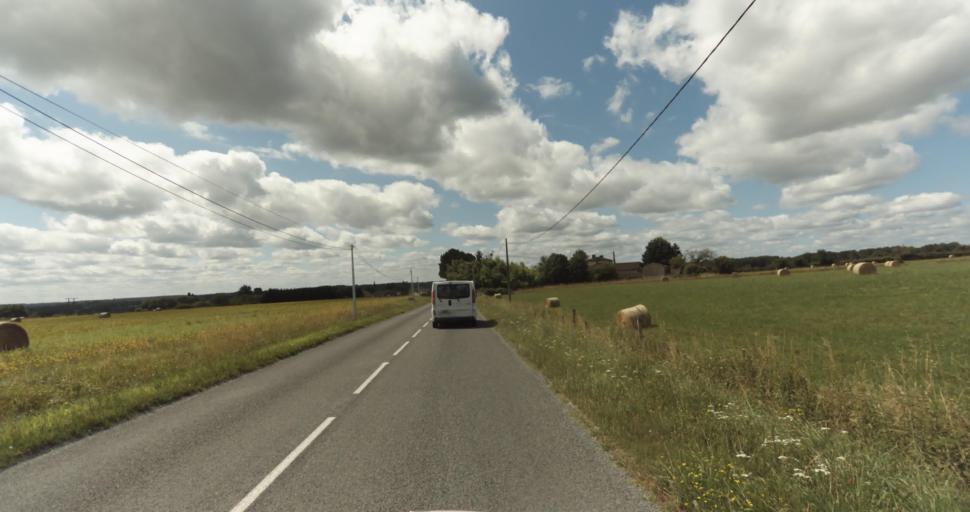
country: FR
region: Aquitaine
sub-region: Departement de la Gironde
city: Bazas
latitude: 44.4444
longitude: -0.2065
